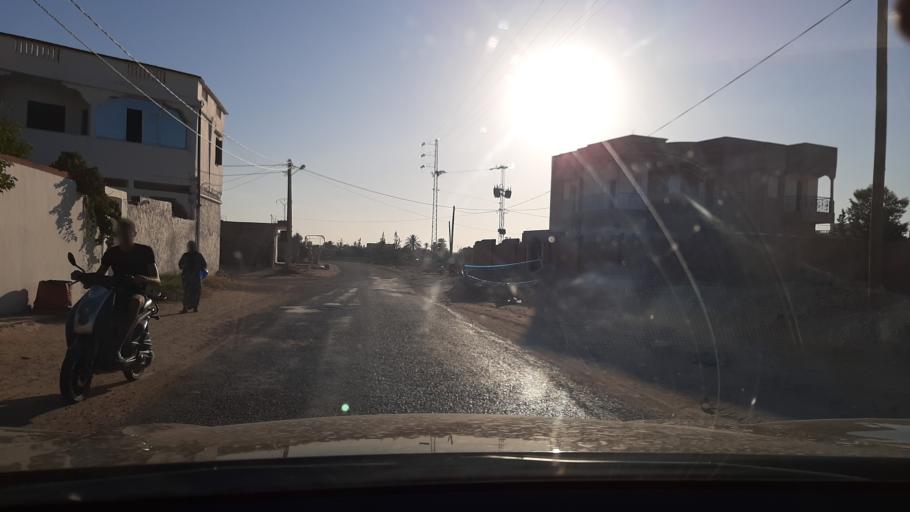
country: TN
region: Qabis
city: Matmata
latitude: 33.6195
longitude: 10.2710
